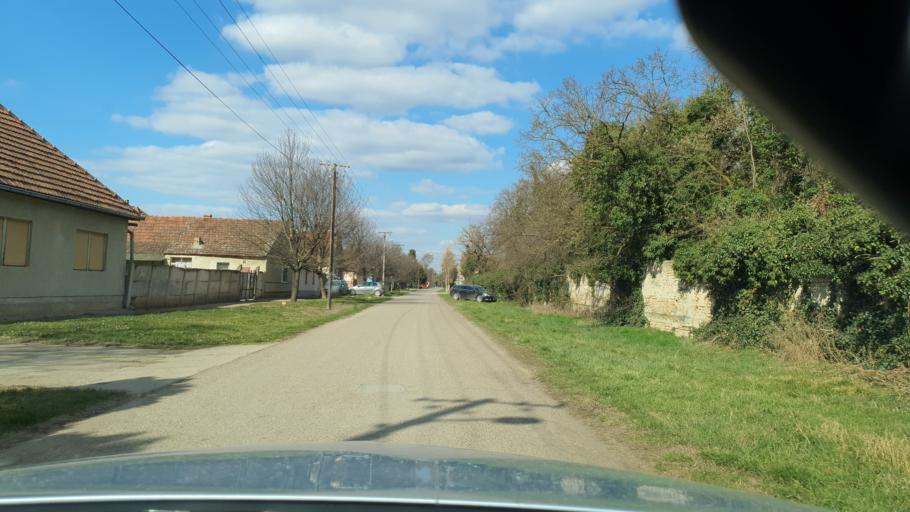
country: RS
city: Kulpin
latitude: 45.4029
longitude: 19.5859
